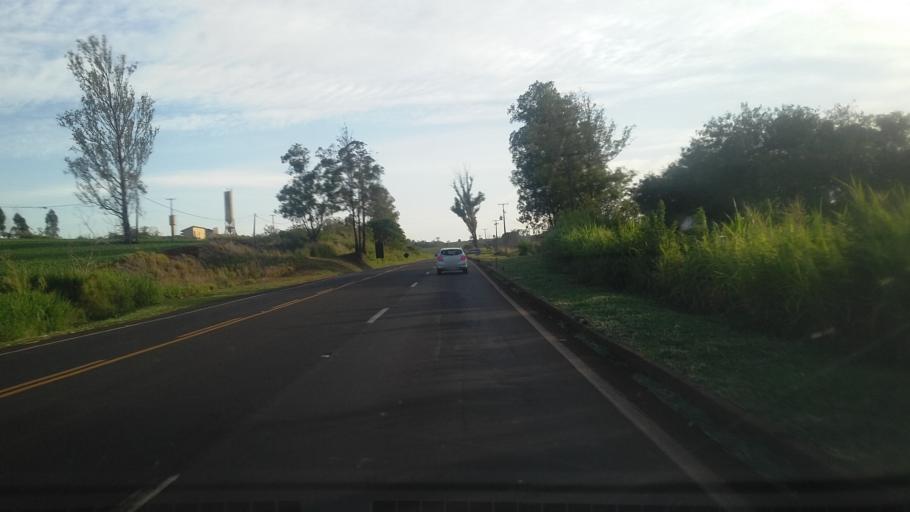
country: BR
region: Parana
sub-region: Assai
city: Assai
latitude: -23.2278
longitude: -50.6767
